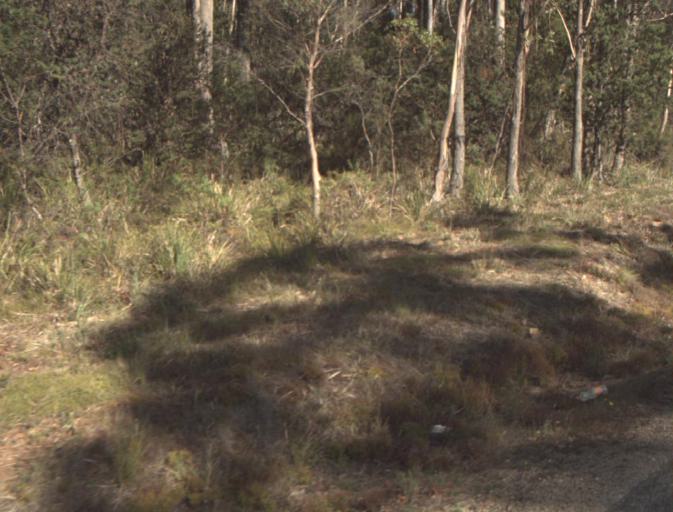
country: AU
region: Tasmania
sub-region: Launceston
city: Mayfield
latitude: -41.3189
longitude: 147.1903
